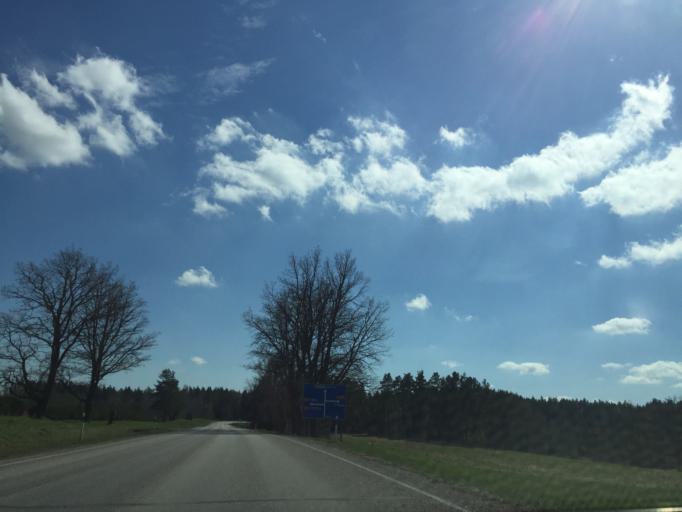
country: EE
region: Valgamaa
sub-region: Torva linn
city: Torva
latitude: 58.0164
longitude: 26.1624
